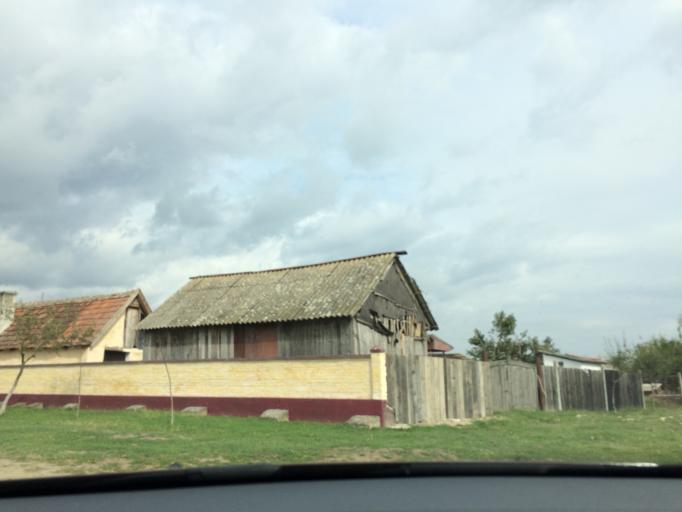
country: RO
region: Timis
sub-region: Comuna Cheveresu Mare
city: Cheveresu Mare
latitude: 45.7276
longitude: 21.4915
